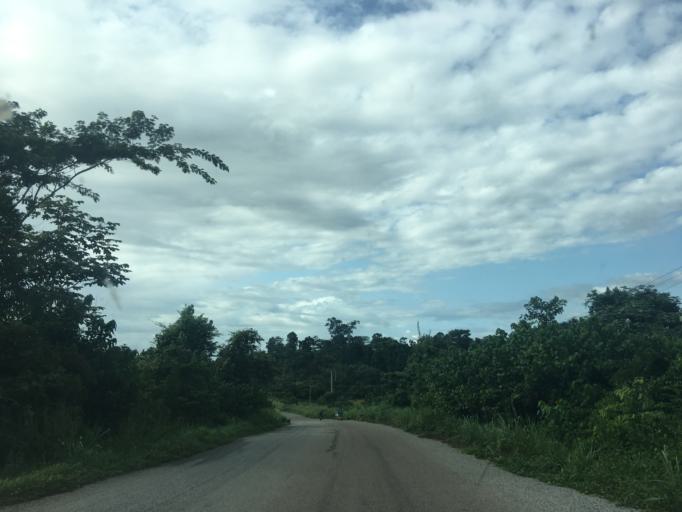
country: GH
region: Western
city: Wassa-Akropong
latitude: 6.0117
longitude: -2.4044
